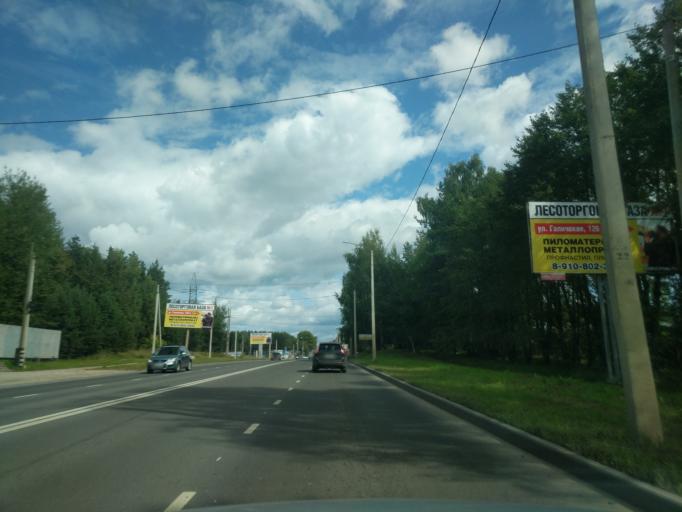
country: RU
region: Kostroma
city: Oktyabr'skiy
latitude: 57.7808
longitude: 40.9861
